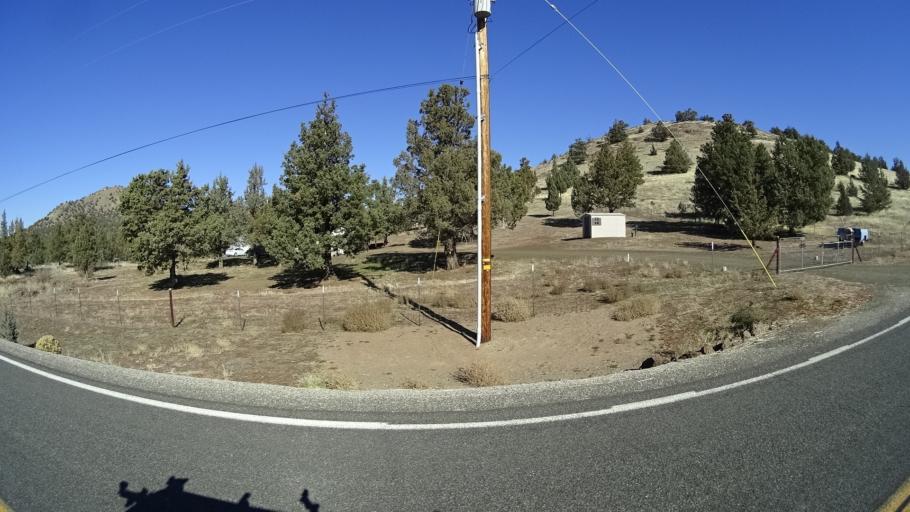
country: US
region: California
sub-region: Siskiyou County
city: Montague
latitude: 41.6591
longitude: -122.3753
